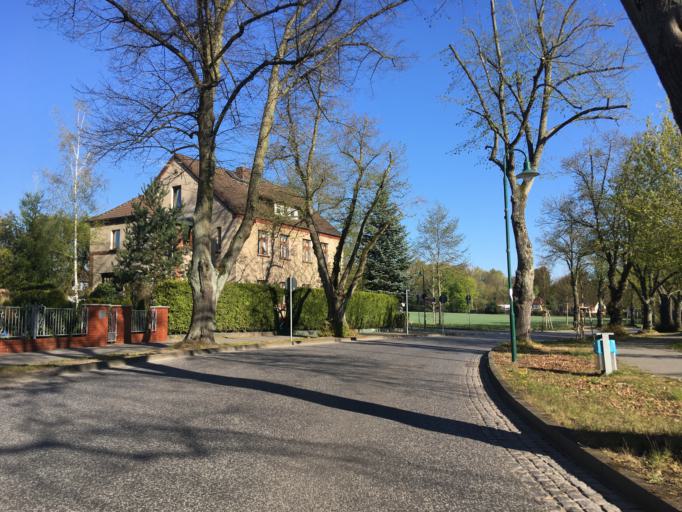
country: DE
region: Berlin
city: Buch
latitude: 52.6607
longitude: 13.5306
